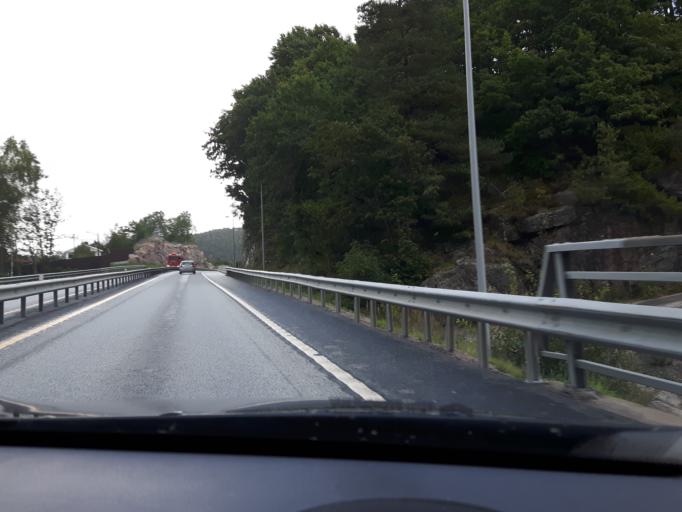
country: NO
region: Vest-Agder
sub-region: Songdalen
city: Nodeland
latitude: 58.1229
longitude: 7.8458
